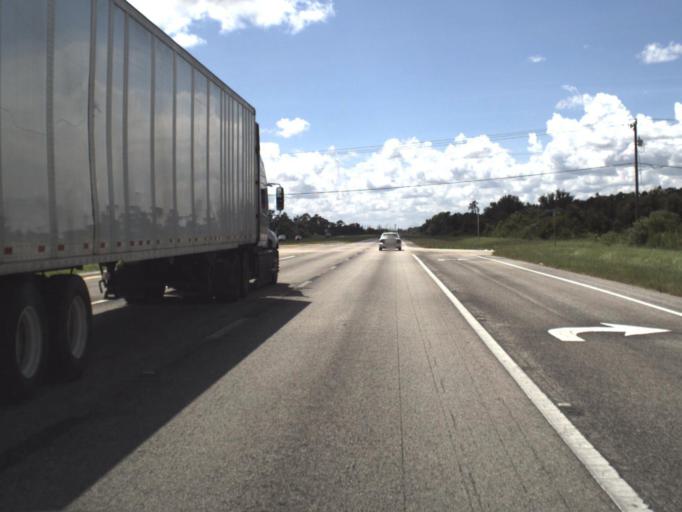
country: US
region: Florida
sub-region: Charlotte County
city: Harbour Heights
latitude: 27.0067
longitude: -81.9589
